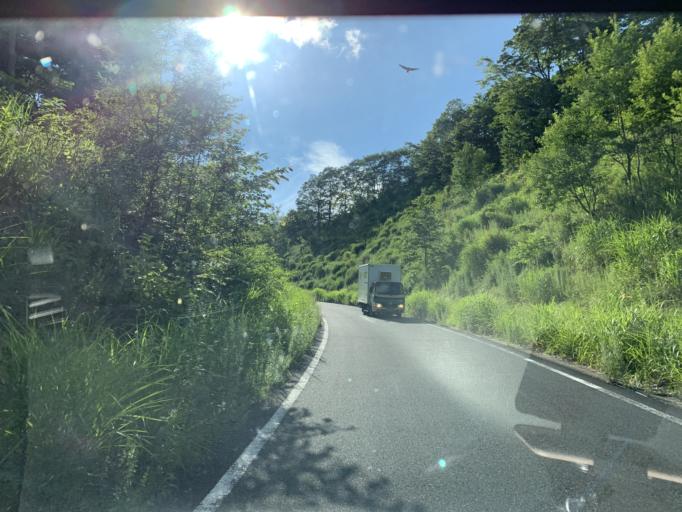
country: JP
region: Iwate
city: Ichinoseki
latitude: 38.9062
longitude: 140.8501
